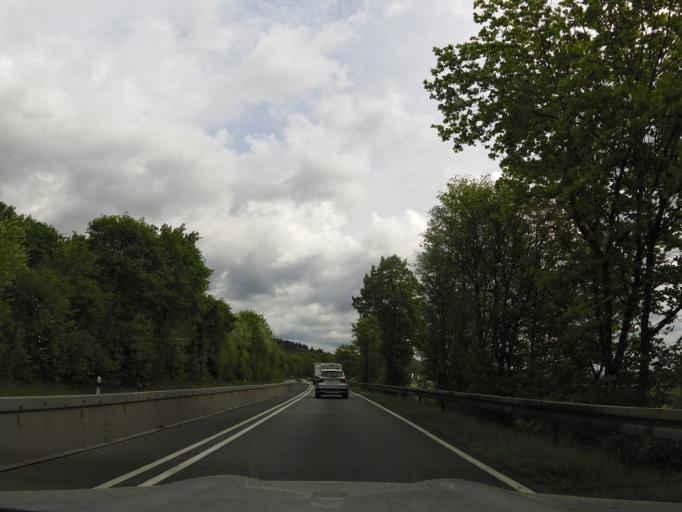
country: DE
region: Hesse
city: Leun
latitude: 50.5434
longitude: 8.3761
